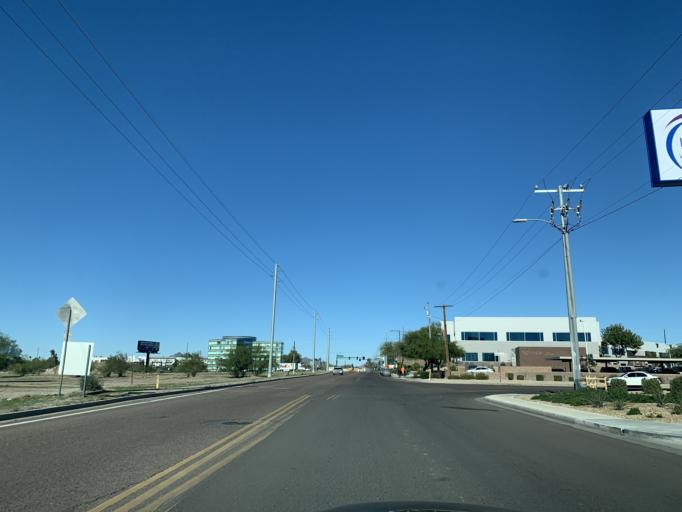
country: US
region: Arizona
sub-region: Maricopa County
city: Tempe Junction
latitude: 33.4450
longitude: -111.9784
